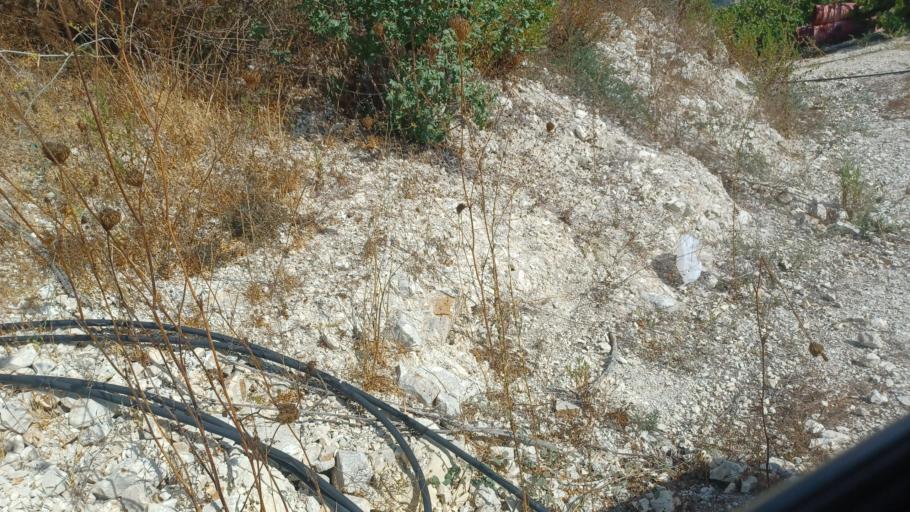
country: CY
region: Pafos
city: Tala
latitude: 34.8687
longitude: 32.4772
